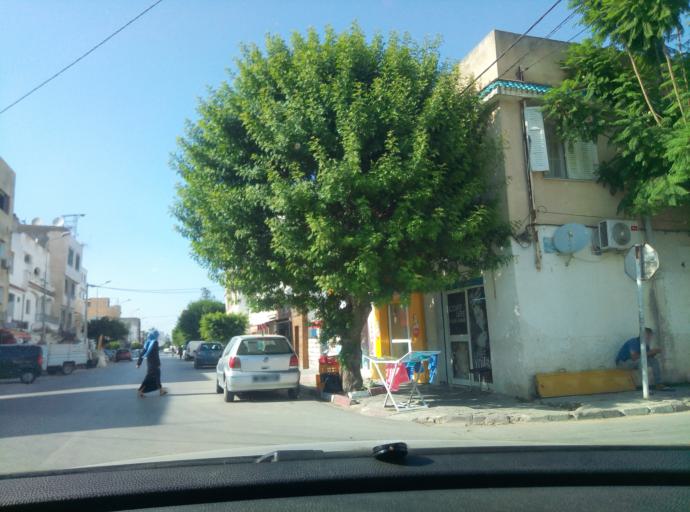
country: TN
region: Tunis
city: La Goulette
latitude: 36.8523
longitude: 10.2618
